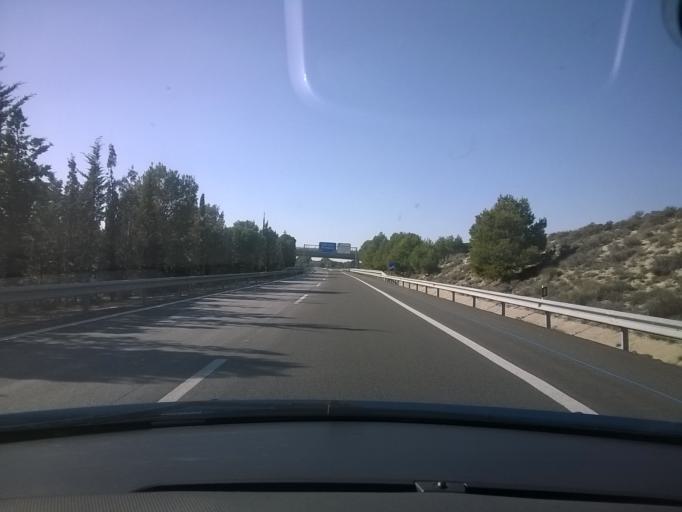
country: ES
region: Aragon
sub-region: Provincia de Zaragoza
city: Bujaraloz
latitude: 41.5247
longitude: -0.1719
